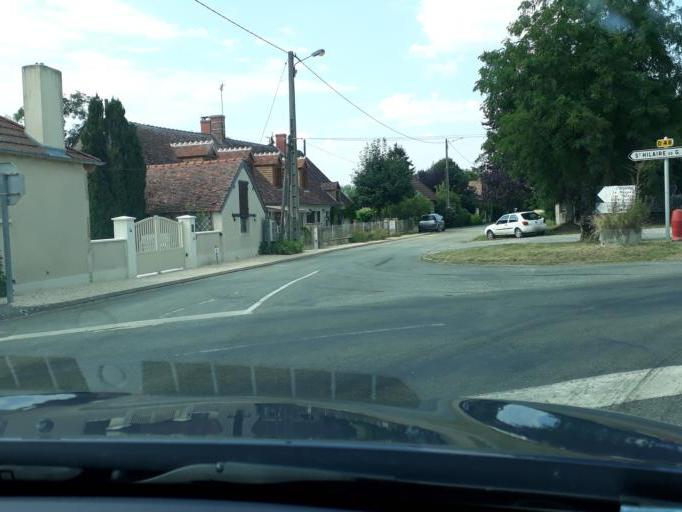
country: FR
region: Centre
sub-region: Departement du Cher
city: Jouet-sur-l'Aubois
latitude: 47.0153
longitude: 2.9082
